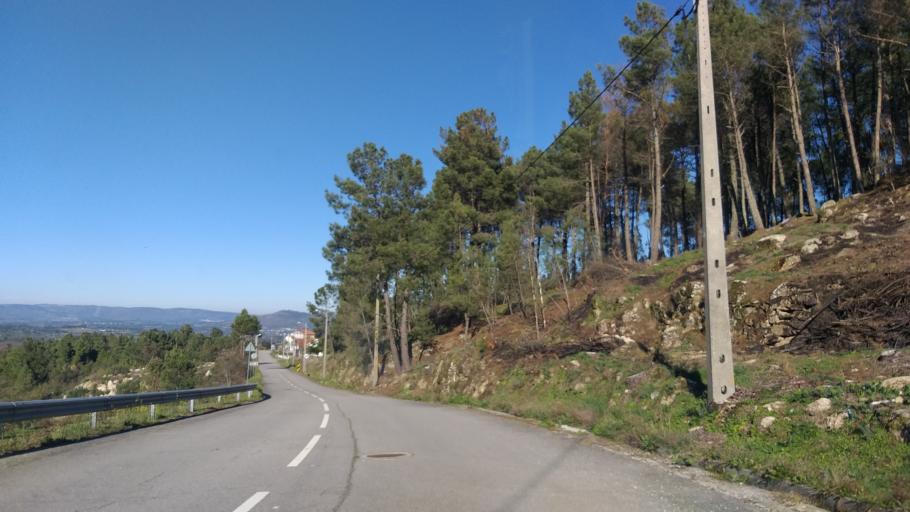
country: PT
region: Guarda
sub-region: Celorico da Beira
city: Celorico da Beira
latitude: 40.5873
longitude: -7.3604
